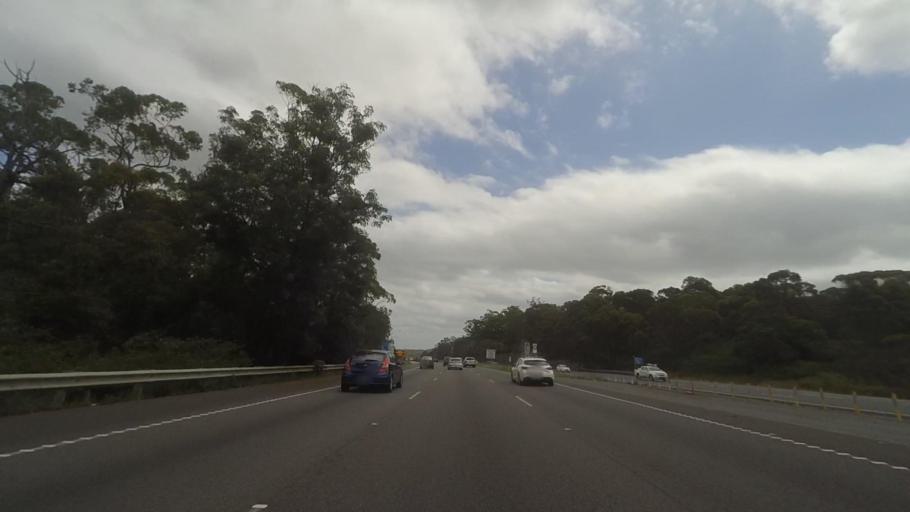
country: AU
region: New South Wales
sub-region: Gosford Shire
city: Point Clare
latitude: -33.4290
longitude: 151.2252
